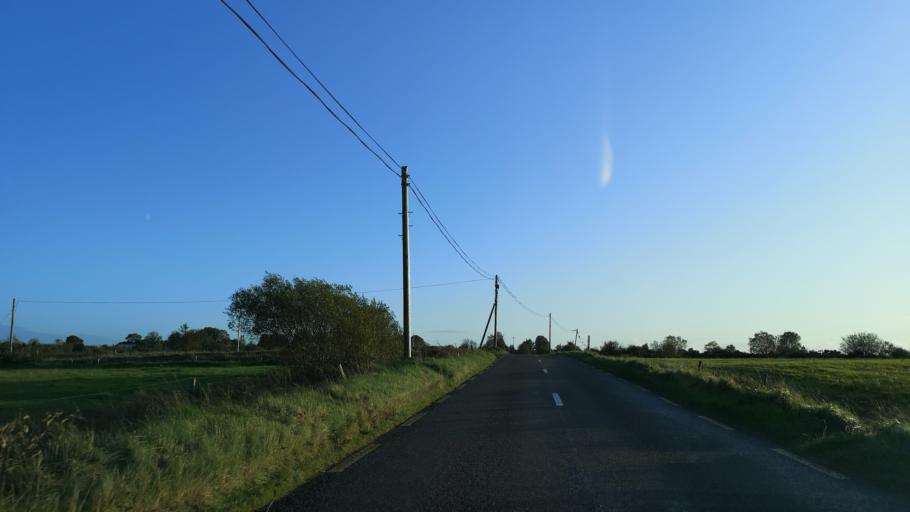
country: IE
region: Connaught
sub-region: Roscommon
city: Castlerea
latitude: 53.7046
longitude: -8.5658
